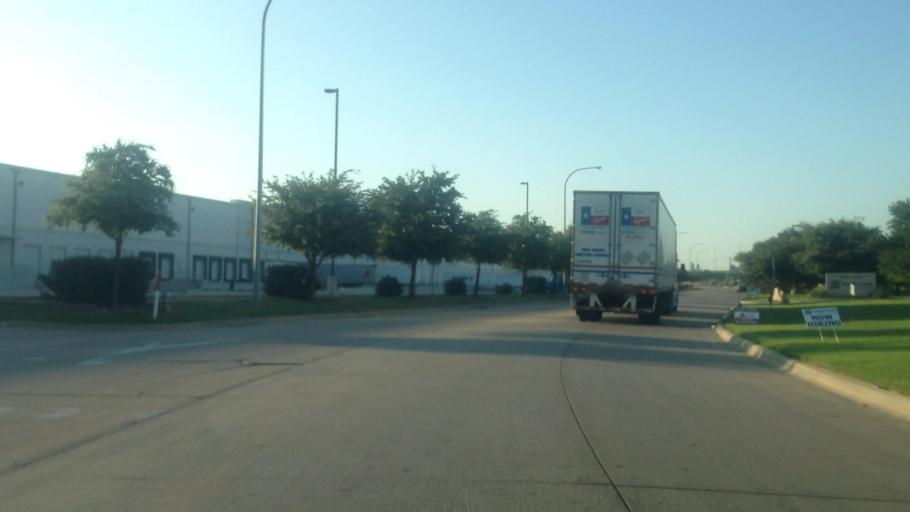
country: US
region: Texas
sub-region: Tarrant County
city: Saginaw
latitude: 32.8345
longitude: -97.3556
